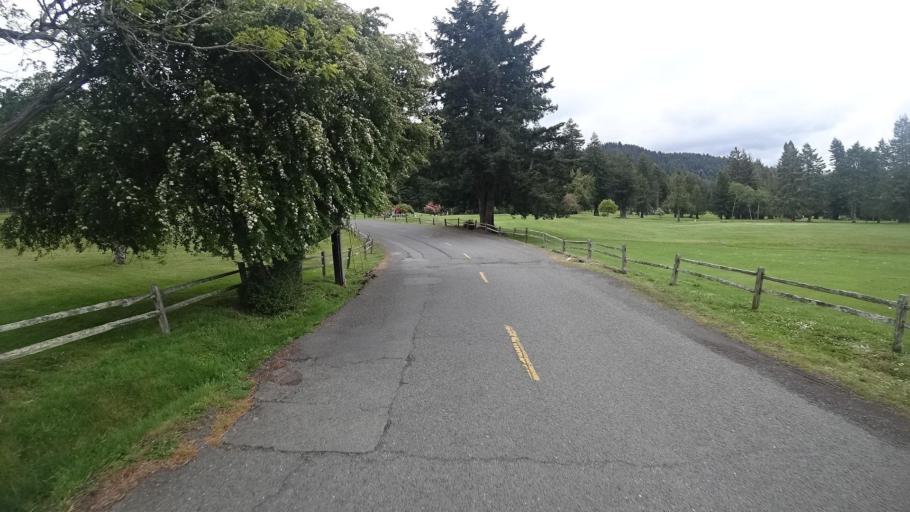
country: US
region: California
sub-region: Humboldt County
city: Bayside
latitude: 40.8460
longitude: -124.0491
